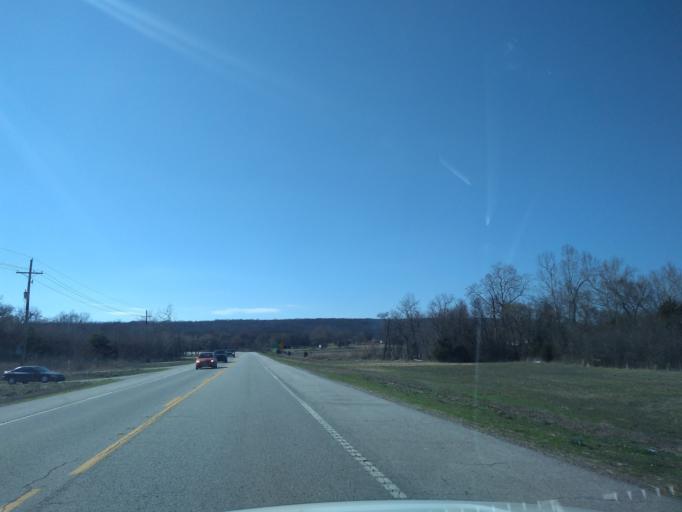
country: US
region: Arkansas
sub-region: Washington County
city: Prairie Grove
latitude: 35.9603
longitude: -94.3631
